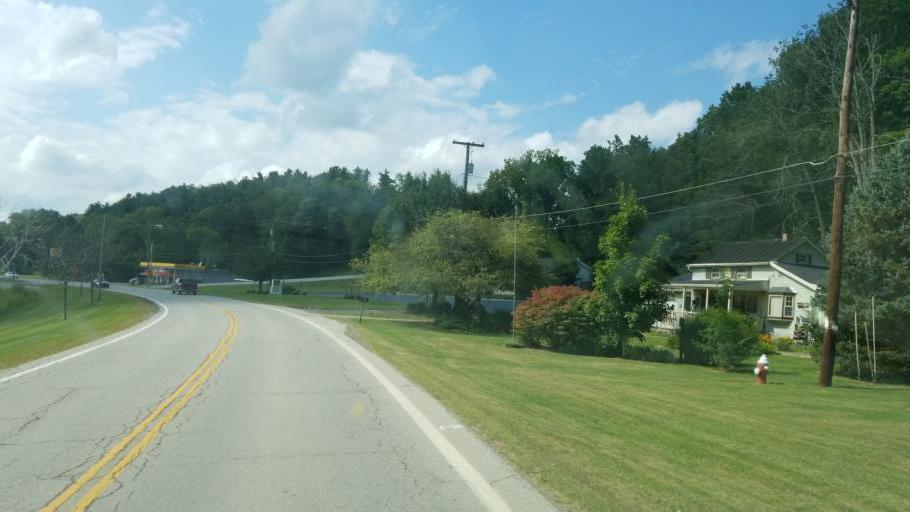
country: US
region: Ohio
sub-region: Sandusky County
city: Bellville
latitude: 40.6242
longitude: -82.5079
